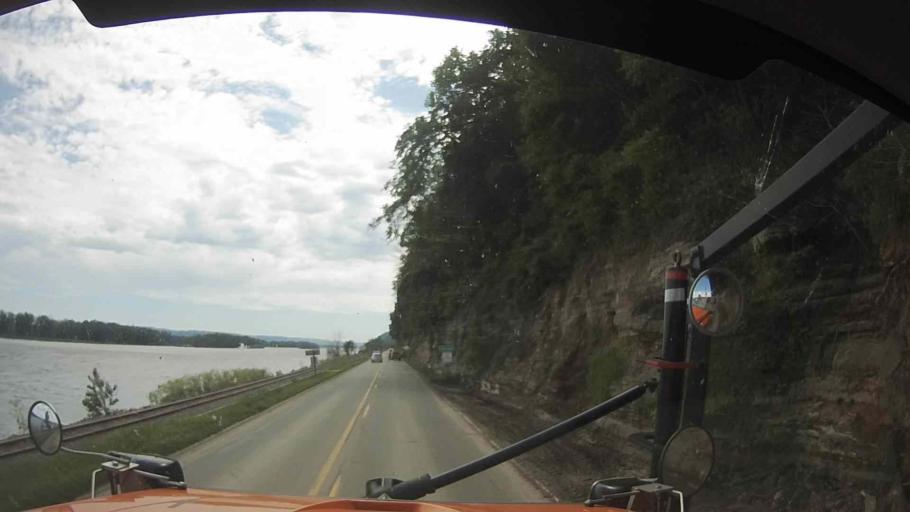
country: US
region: Wisconsin
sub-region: Crawford County
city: Prairie du Chien
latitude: 43.0380
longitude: -91.1764
